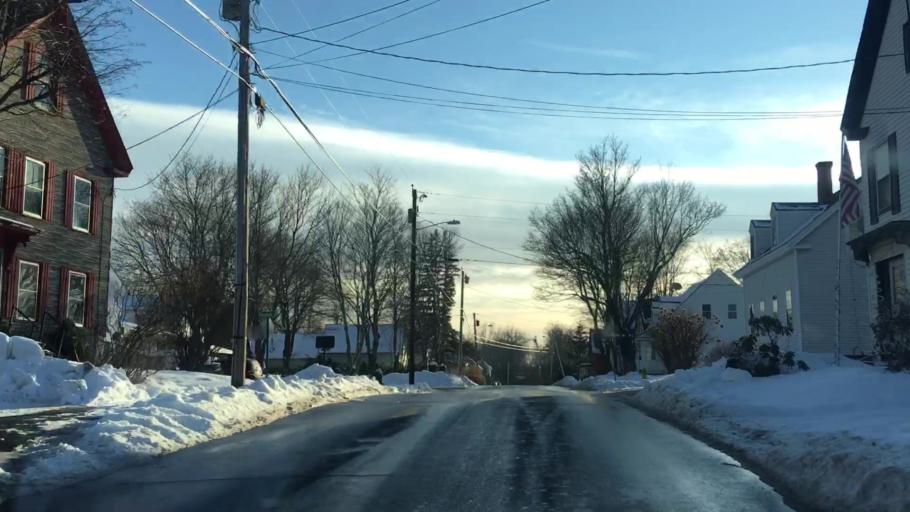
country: US
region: Maine
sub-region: Kennebec County
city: Gardiner
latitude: 44.2315
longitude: -69.7822
